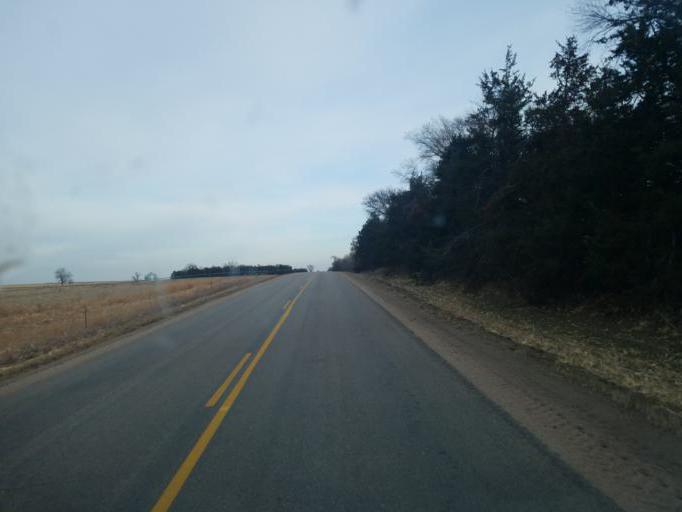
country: US
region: Nebraska
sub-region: Knox County
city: Creighton
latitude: 42.4661
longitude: -98.2265
